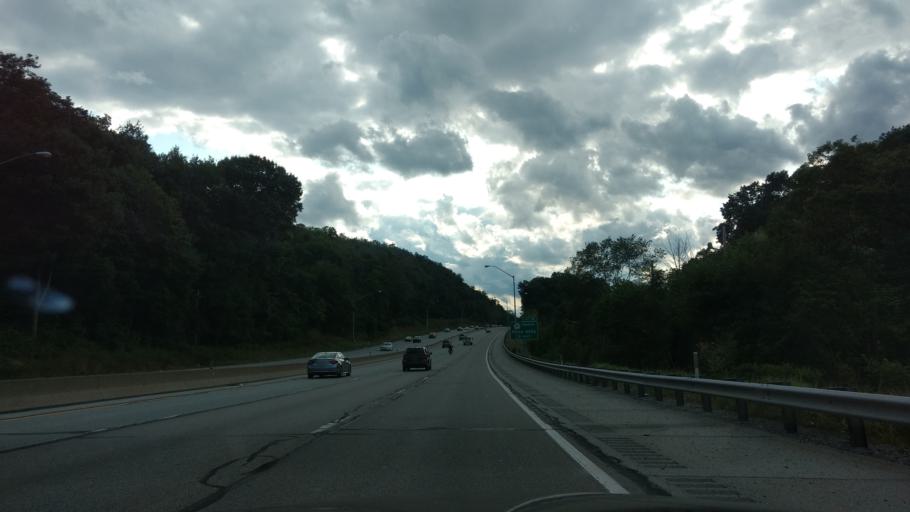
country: US
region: Pennsylvania
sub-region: Allegheny County
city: Monroeville
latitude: 40.4423
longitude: -79.7870
